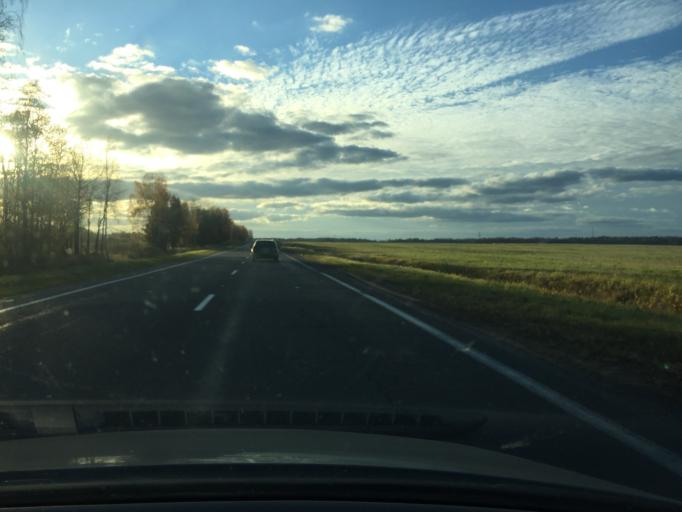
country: BY
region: Vitebsk
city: Vyerkhnyadzvinsk
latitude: 55.8377
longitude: 27.8458
